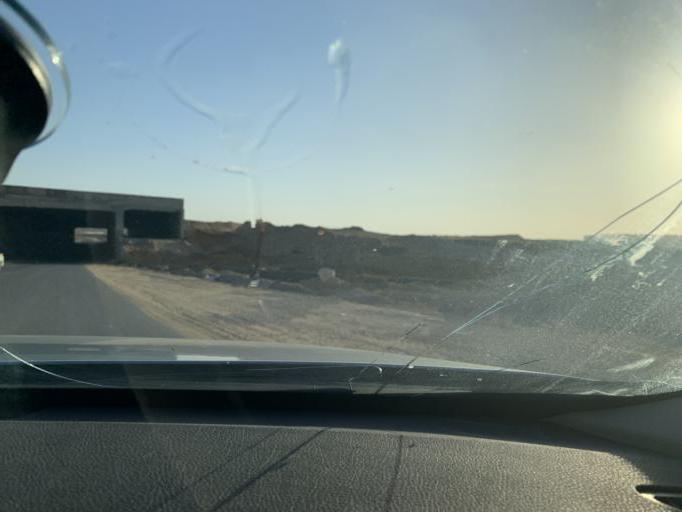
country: EG
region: Muhafazat al Qalyubiyah
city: Al Khankah
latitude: 30.0213
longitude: 31.6751
